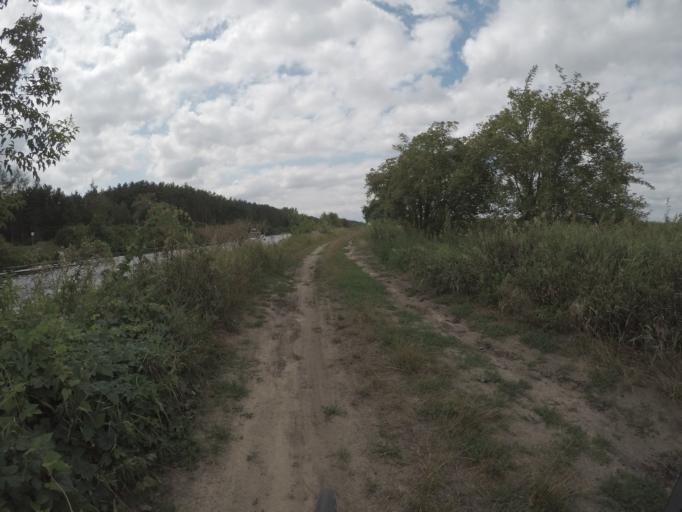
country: DE
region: Brandenburg
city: Falkensee
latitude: 52.6074
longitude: 13.0699
